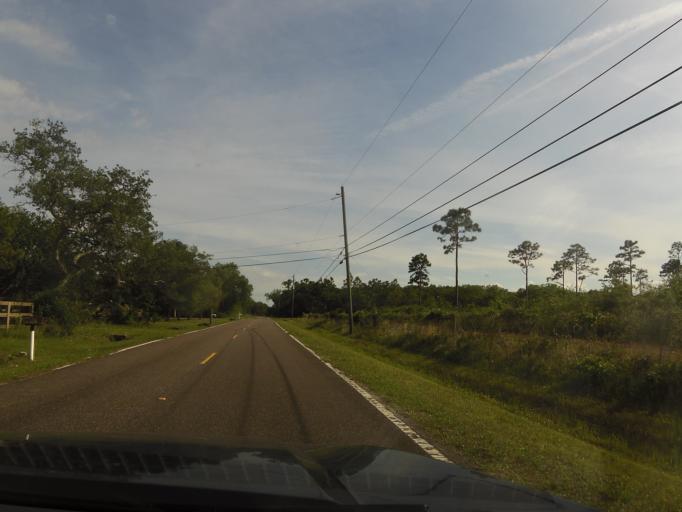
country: US
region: Florida
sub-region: Duval County
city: Atlantic Beach
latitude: 30.4694
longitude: -81.4864
